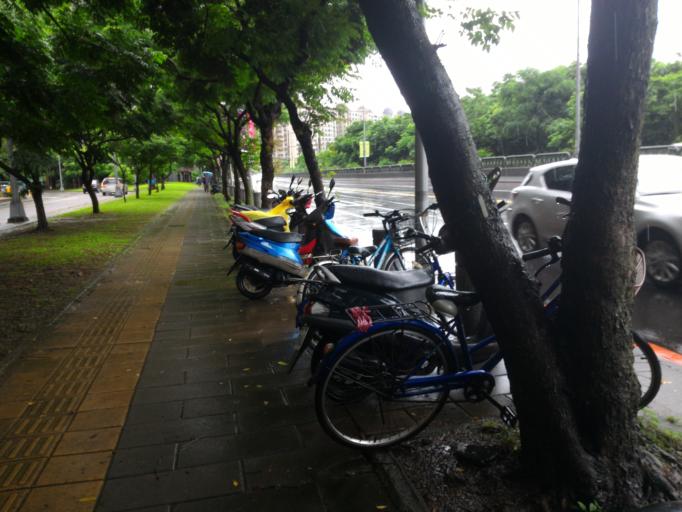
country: TW
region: Taiwan
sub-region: Taoyuan
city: Taoyuan
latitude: 24.9414
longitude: 121.3709
